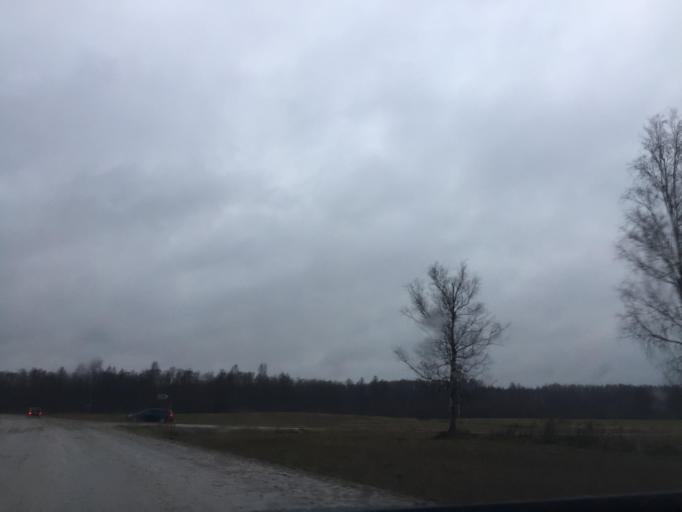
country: LV
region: Salacgrivas
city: Salacgriva
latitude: 57.7713
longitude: 24.5261
